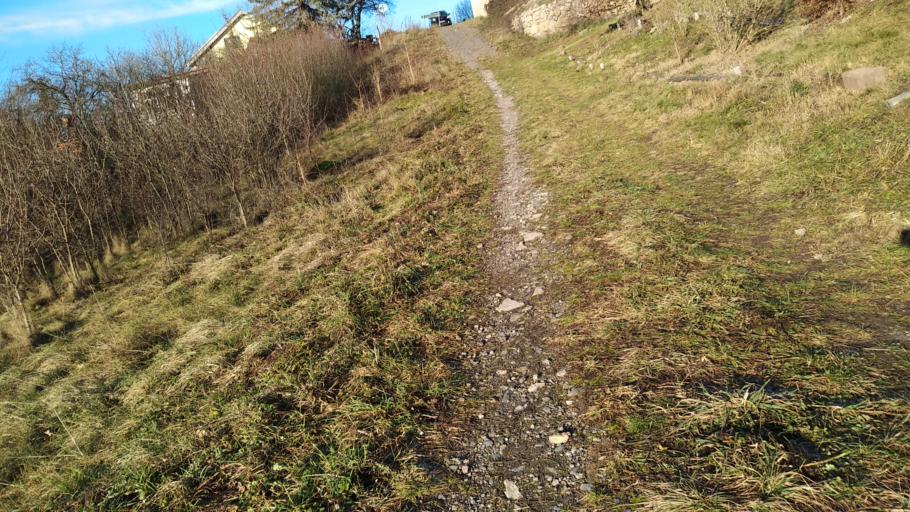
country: DE
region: Thuringia
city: Bad Blankenburg
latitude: 50.6885
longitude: 11.2574
